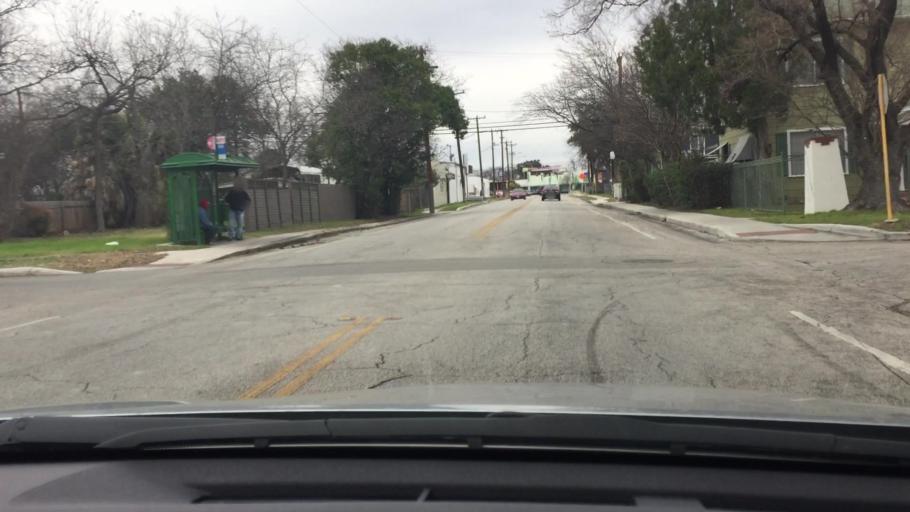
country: US
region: Texas
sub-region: Bexar County
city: Balcones Heights
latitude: 29.4591
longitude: -98.5232
